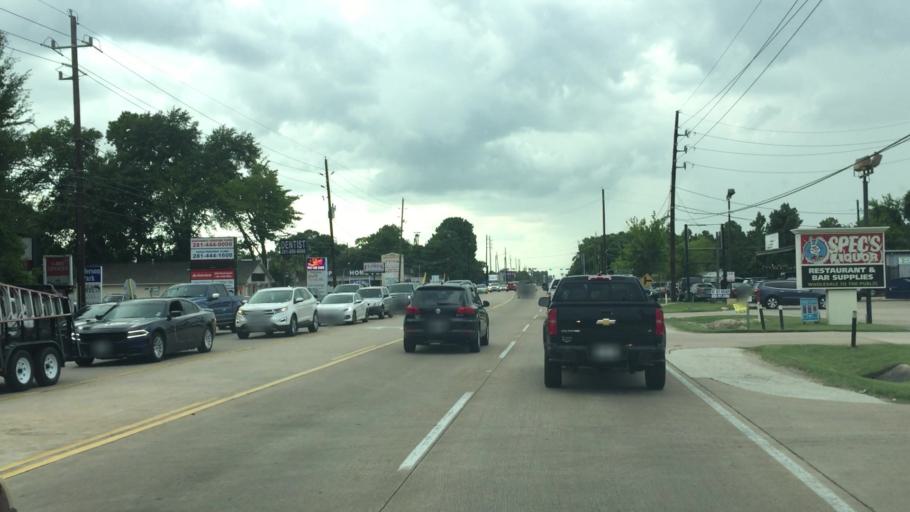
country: US
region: Texas
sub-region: Harris County
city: Hudson
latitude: 29.9897
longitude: -95.4997
